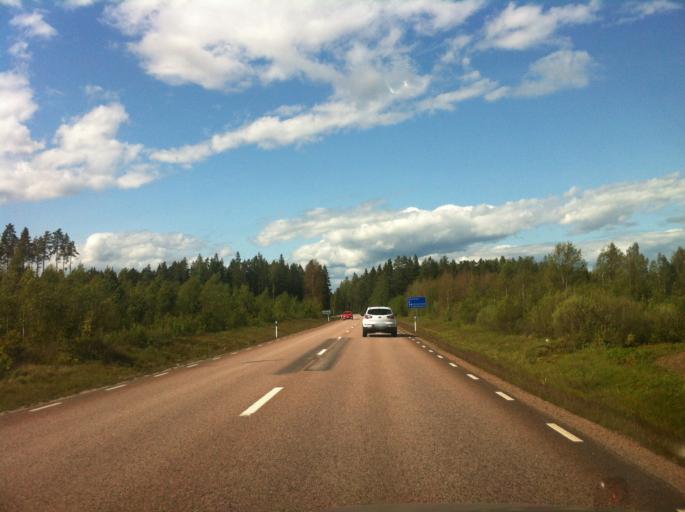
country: SE
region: Vaermland
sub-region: Kristinehamns Kommun
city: Bjorneborg
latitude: 59.2472
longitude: 14.1778
